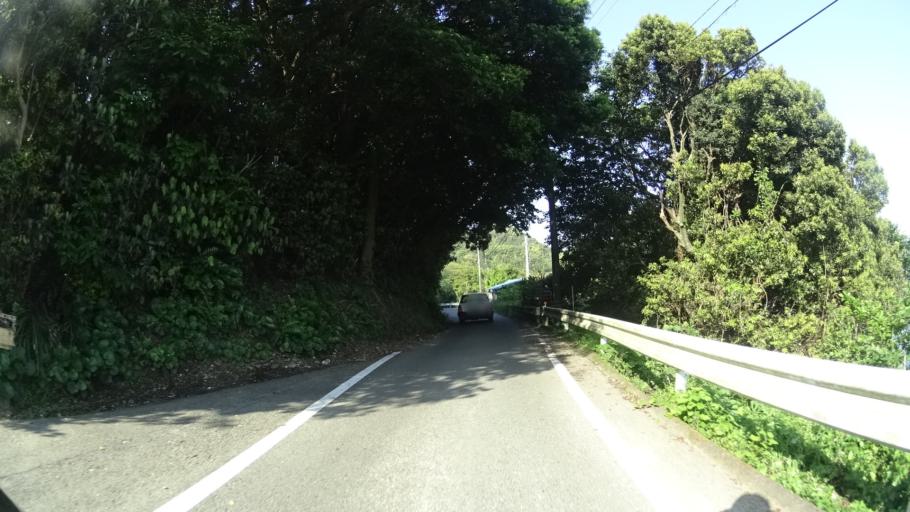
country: JP
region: Oita
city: Tsukumiura
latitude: 33.3487
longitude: 132.0275
